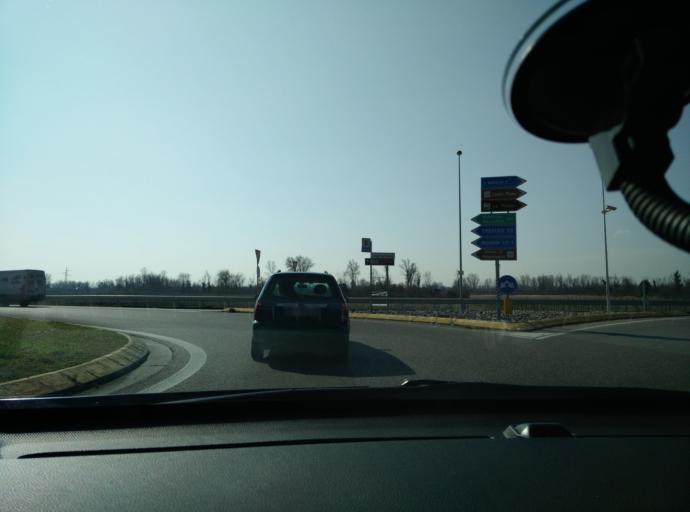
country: IT
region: Veneto
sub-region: Provincia di Treviso
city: San Michele di Piave
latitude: 45.7889
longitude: 12.3536
